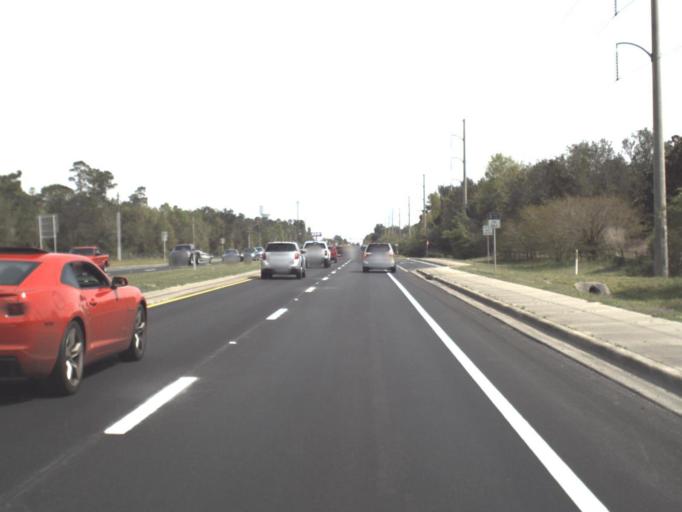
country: US
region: Florida
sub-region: Okaloosa County
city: Niceville
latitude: 30.4940
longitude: -86.4311
